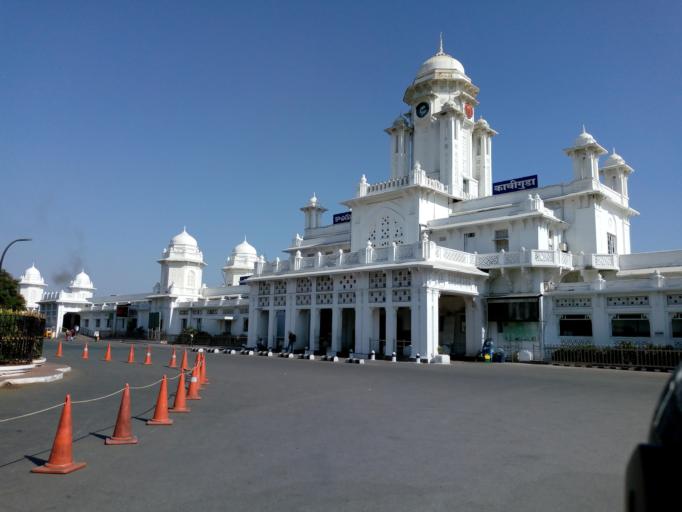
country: IN
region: Telangana
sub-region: Rangareddi
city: Gaddi Annaram
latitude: 17.3894
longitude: 78.4987
